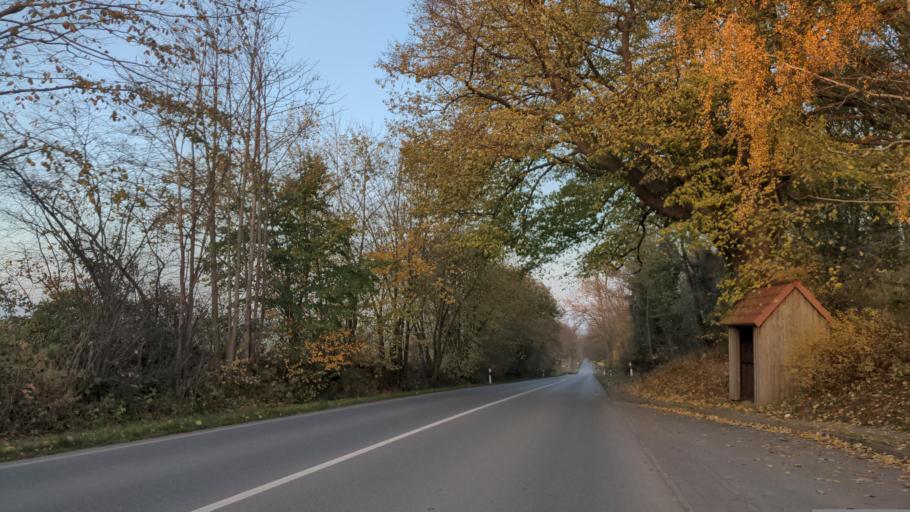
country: DE
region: Schleswig-Holstein
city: Malente
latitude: 54.1104
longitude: 10.5432
